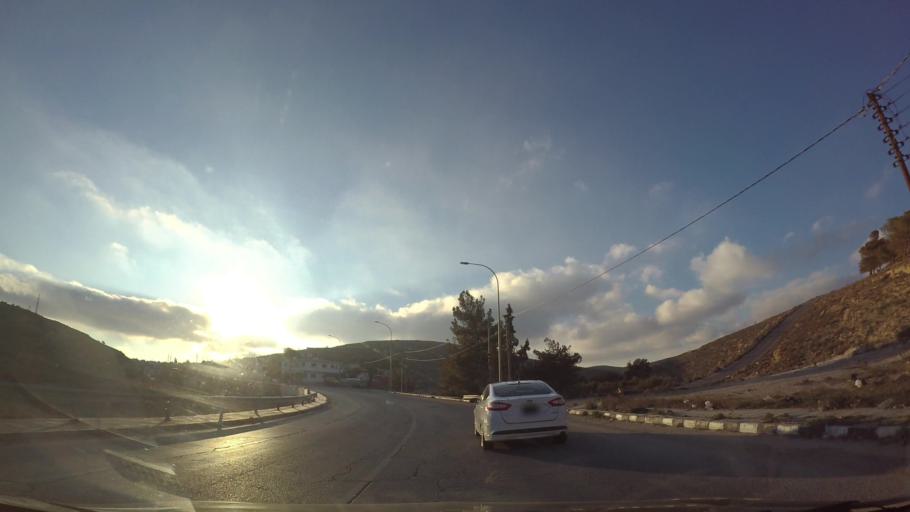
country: JO
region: Ma'an
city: Petra
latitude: 30.5218
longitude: 35.5505
